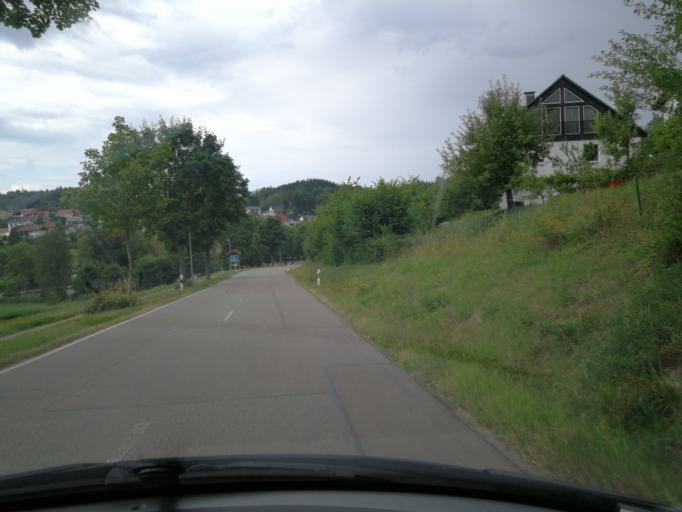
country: DE
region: Bavaria
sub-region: Upper Palatinate
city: Falkenstein
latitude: 49.0986
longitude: 12.4813
